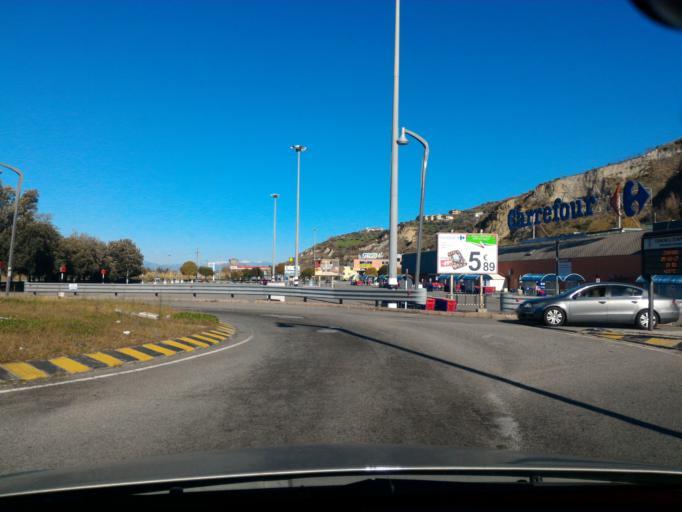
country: IT
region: Calabria
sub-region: Provincia di Cosenza
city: Cosenza
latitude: 39.3113
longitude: 16.2629
